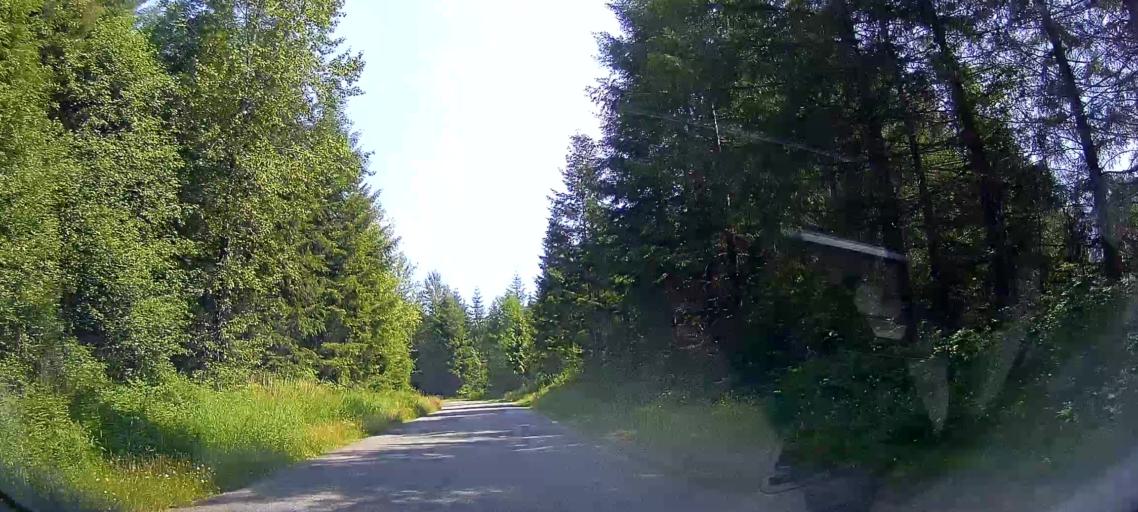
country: US
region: Washington
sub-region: Snohomish County
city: Arlington Heights
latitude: 48.3349
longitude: -122.0202
